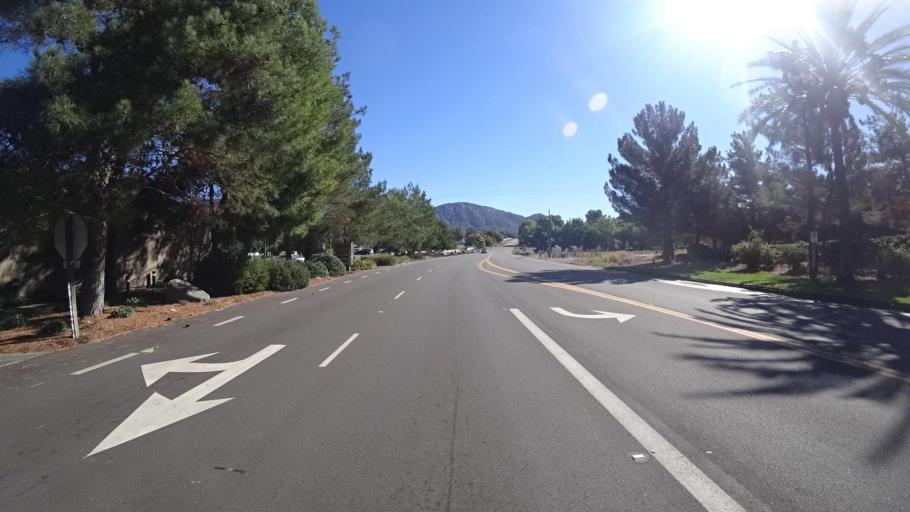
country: US
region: California
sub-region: San Diego County
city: Alpine
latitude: 32.8421
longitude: -116.7029
